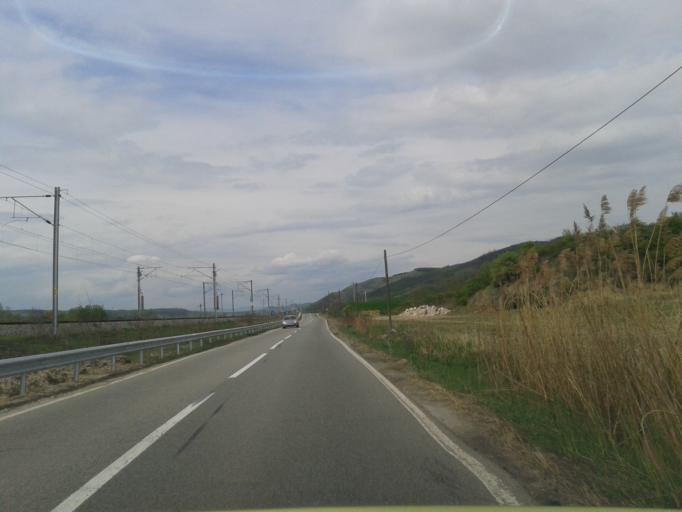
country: RO
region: Alba
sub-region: Comuna Valea Lunga
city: Valea Lunga
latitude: 46.1329
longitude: 24.0101
